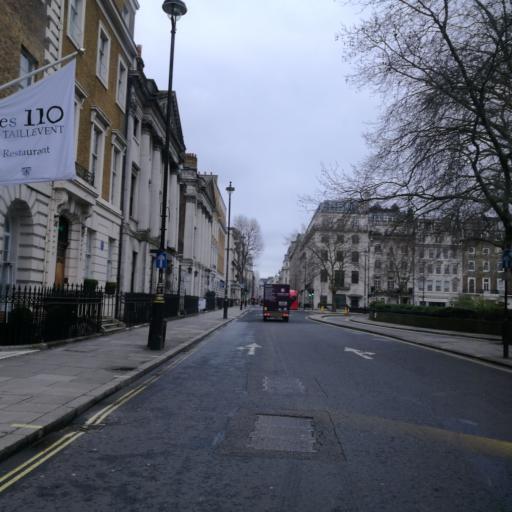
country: GB
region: England
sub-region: Greater London
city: London
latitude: 51.5169
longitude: -0.1459
